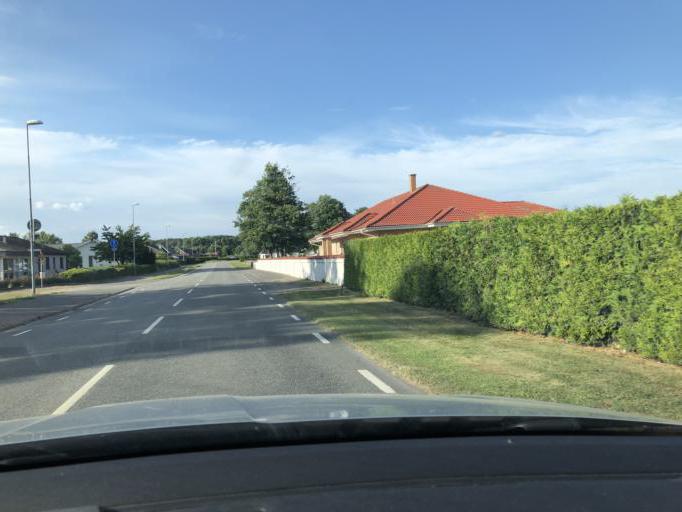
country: SE
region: Blekinge
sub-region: Solvesborgs Kommun
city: Soelvesborg
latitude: 56.0592
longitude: 14.5354
